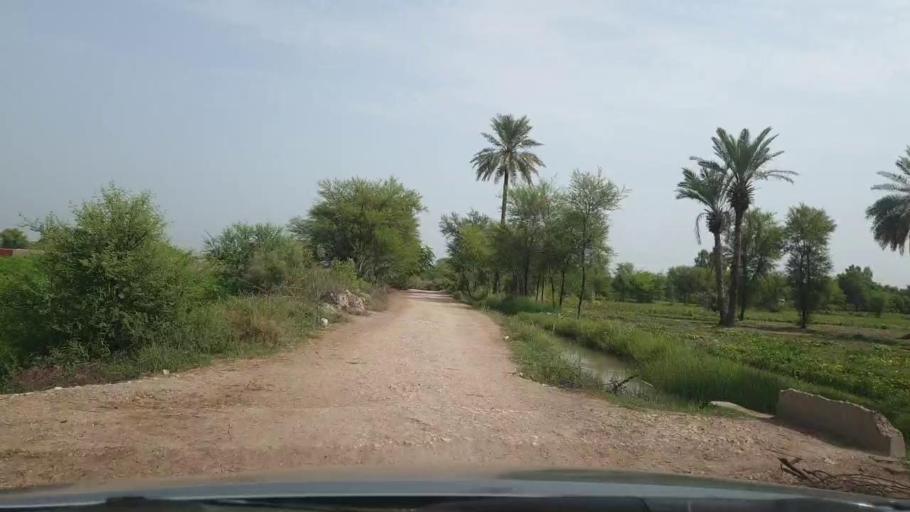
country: PK
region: Sindh
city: Rohri
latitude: 27.6490
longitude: 69.0233
